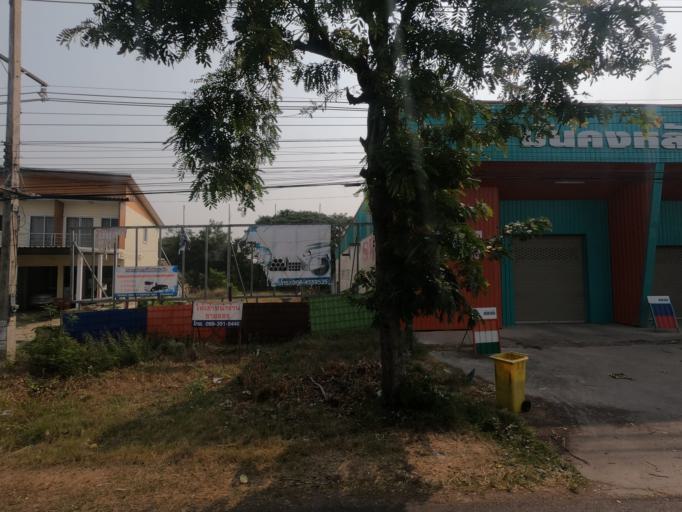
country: TH
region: Khon Kaen
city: Ban Phai
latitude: 16.0462
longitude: 102.7150
